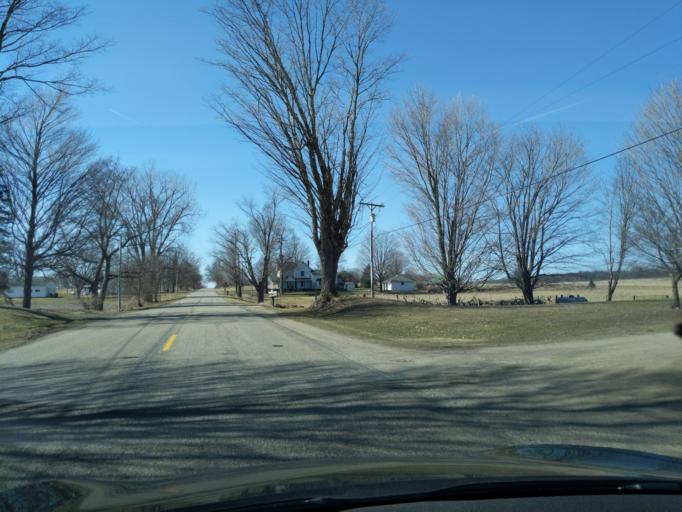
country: US
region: Michigan
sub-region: Eaton County
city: Grand Ledge
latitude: 42.7264
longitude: -84.7617
